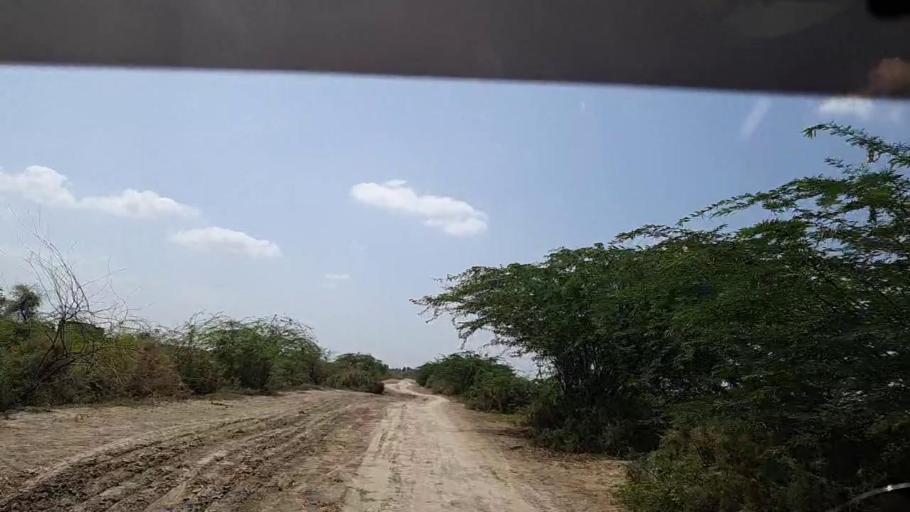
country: PK
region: Sindh
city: Badin
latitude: 24.5547
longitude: 68.7363
